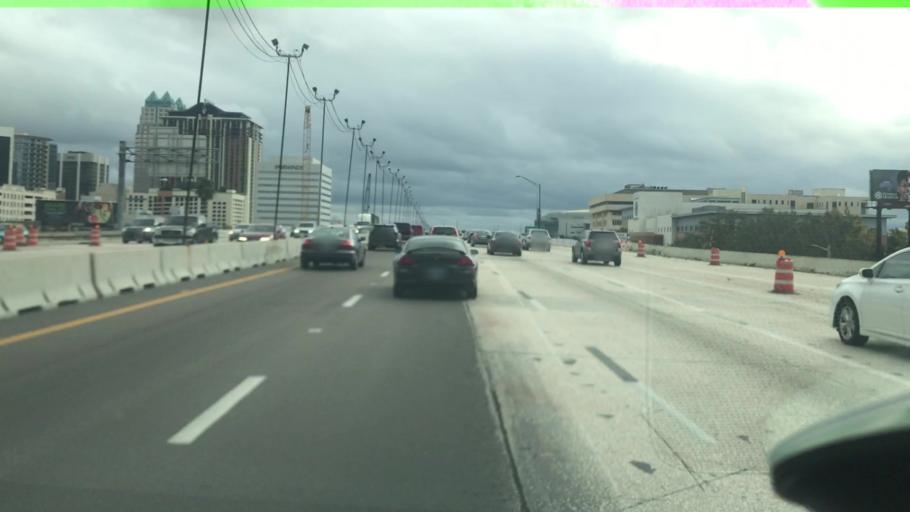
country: US
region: Florida
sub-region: Orange County
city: Orlando
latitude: 28.5471
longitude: -81.3825
